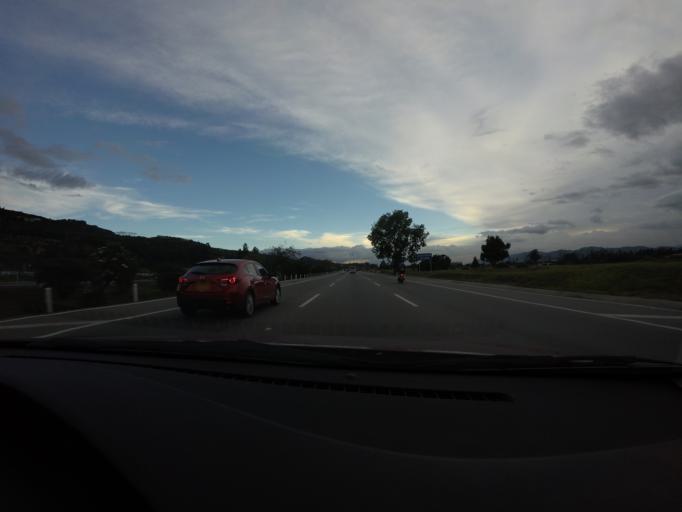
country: CO
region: Cundinamarca
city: Cajica
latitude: 4.8970
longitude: -74.0075
